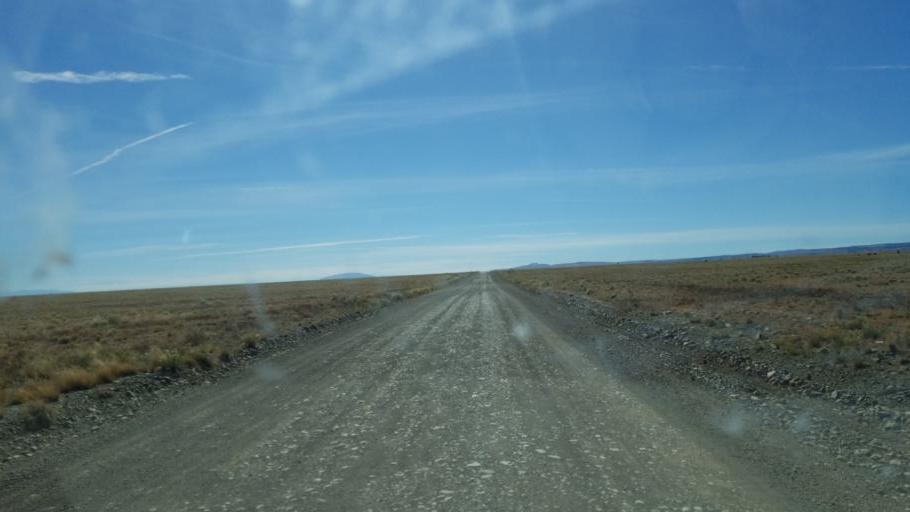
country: US
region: Colorado
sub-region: Rio Grande County
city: Monte Vista
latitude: 37.3679
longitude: -106.1493
